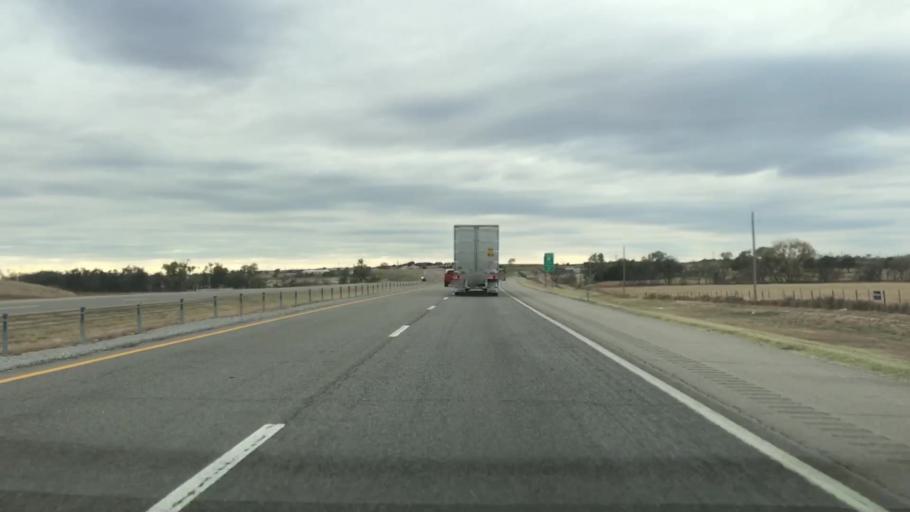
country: US
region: Oklahoma
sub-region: Washita County
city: Burns Flat
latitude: 35.4478
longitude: -99.1633
